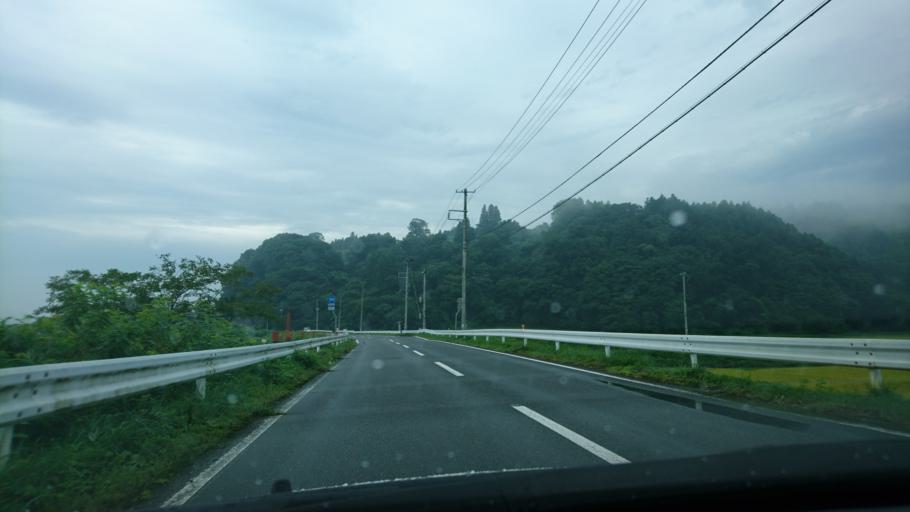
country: JP
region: Iwate
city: Ichinoseki
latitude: 38.8879
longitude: 141.2663
